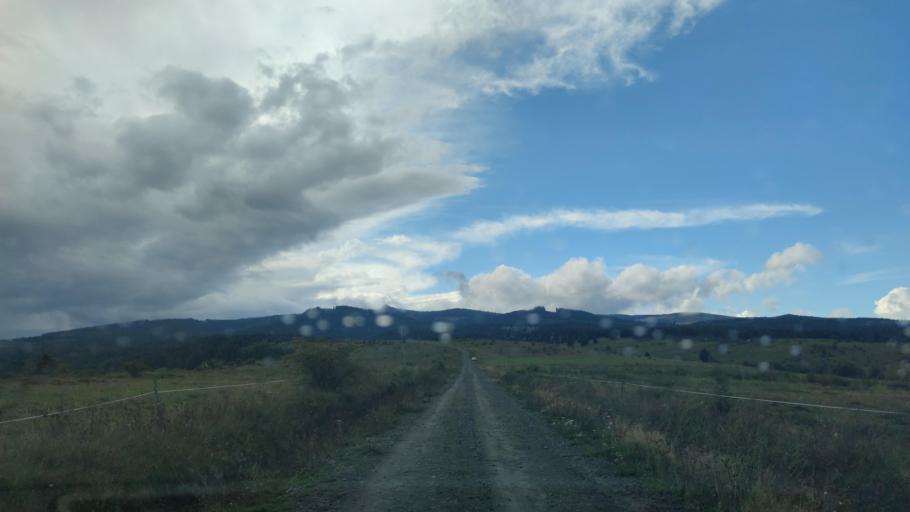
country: RO
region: Harghita
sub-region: Comuna Remetea
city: Remetea
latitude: 46.8160
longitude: 25.3745
